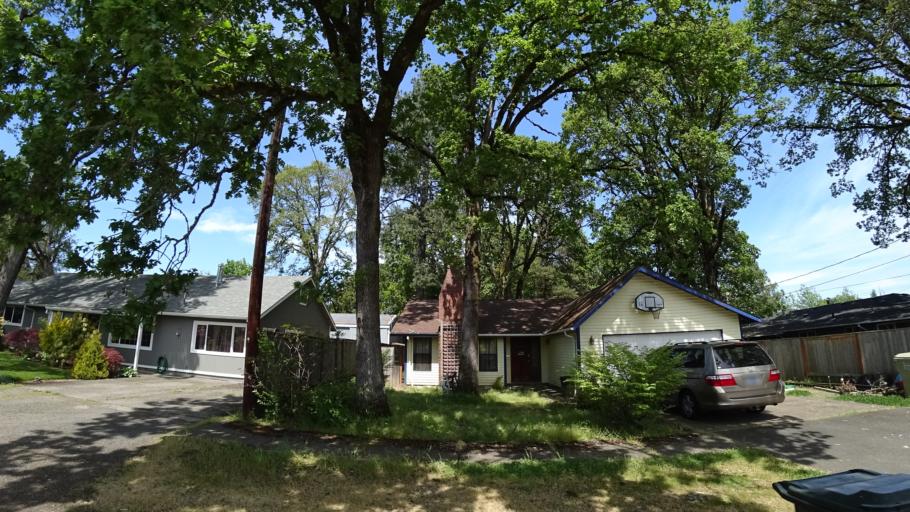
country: US
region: Oregon
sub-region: Washington County
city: Aloha
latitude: 45.4883
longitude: -122.8474
